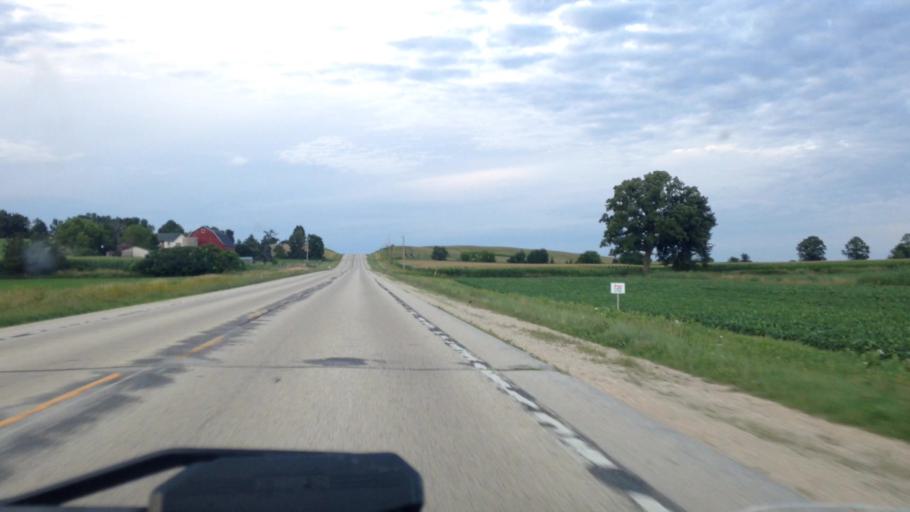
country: US
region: Wisconsin
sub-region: Dodge County
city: Theresa
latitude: 43.4746
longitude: -88.4501
